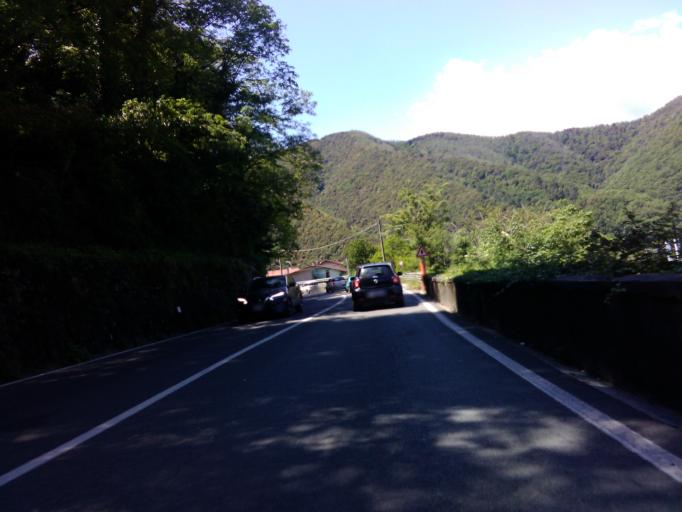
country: IT
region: Tuscany
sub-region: Provincia di Massa-Carrara
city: Albiano Magra
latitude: 44.1846
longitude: 9.9272
